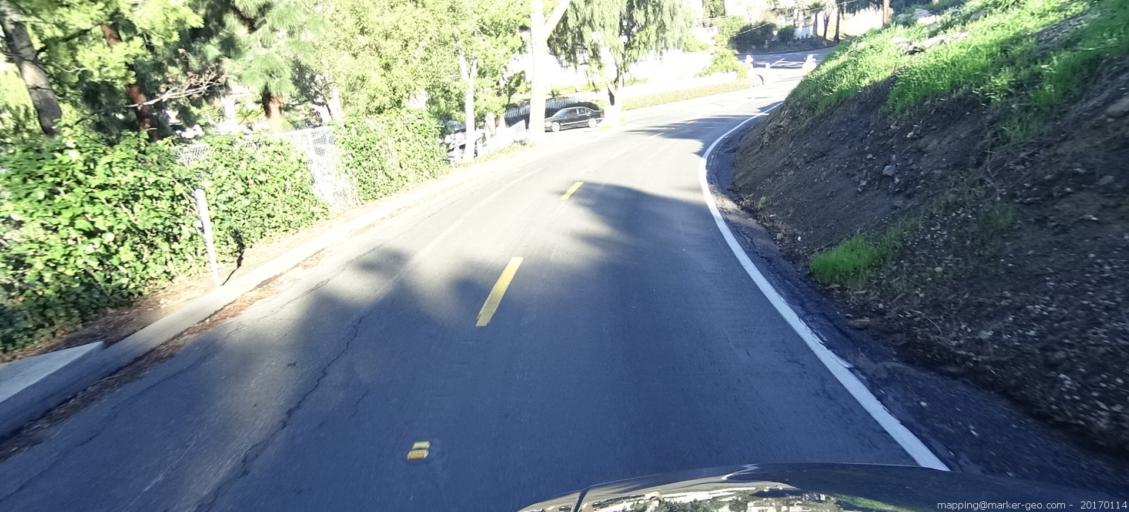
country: US
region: California
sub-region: Orange County
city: North Tustin
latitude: 33.7776
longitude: -117.7971
